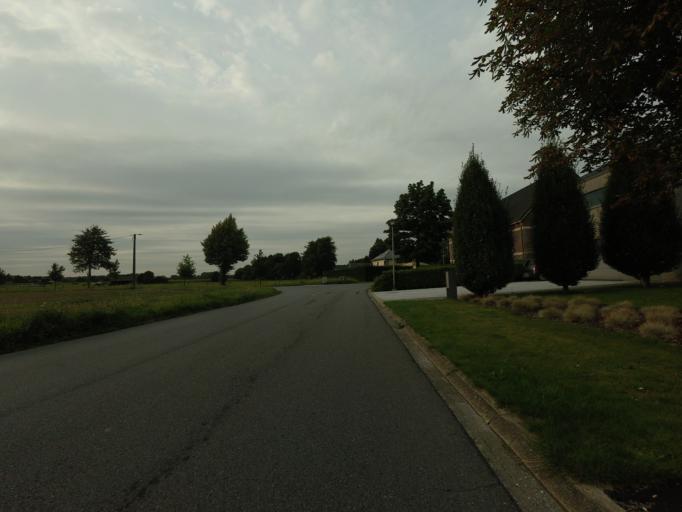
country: BE
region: Flanders
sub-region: Provincie Vlaams-Brabant
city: Kampenhout
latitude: 50.9426
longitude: 4.5596
